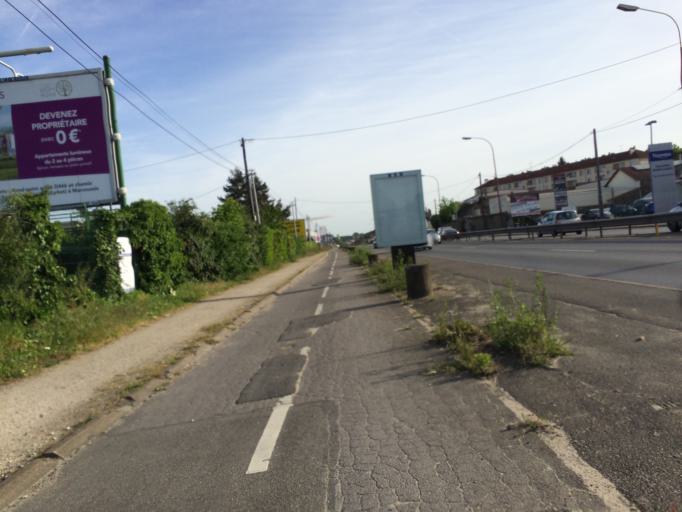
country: FR
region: Ile-de-France
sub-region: Departement de l'Essonne
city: Montlhery
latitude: 48.6464
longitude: 2.2708
